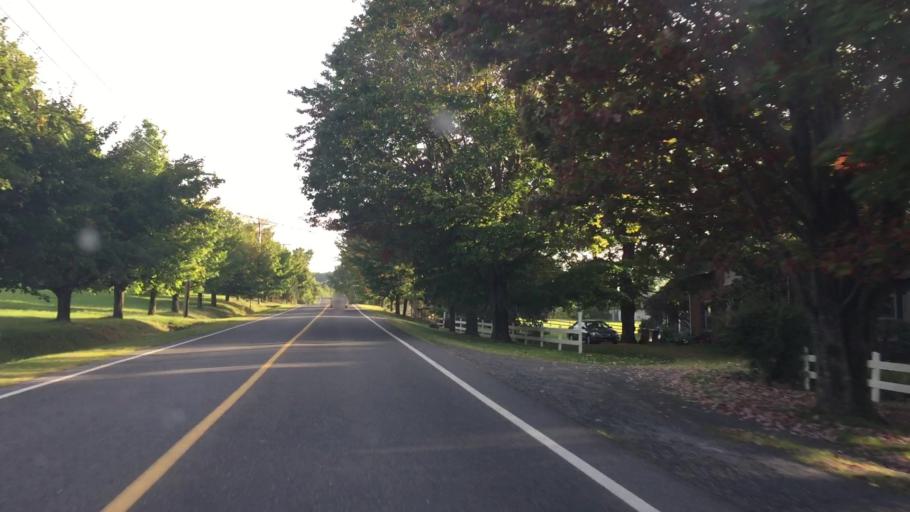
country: CA
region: Quebec
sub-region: Monteregie
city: Bromont
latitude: 45.3020
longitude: -72.6599
